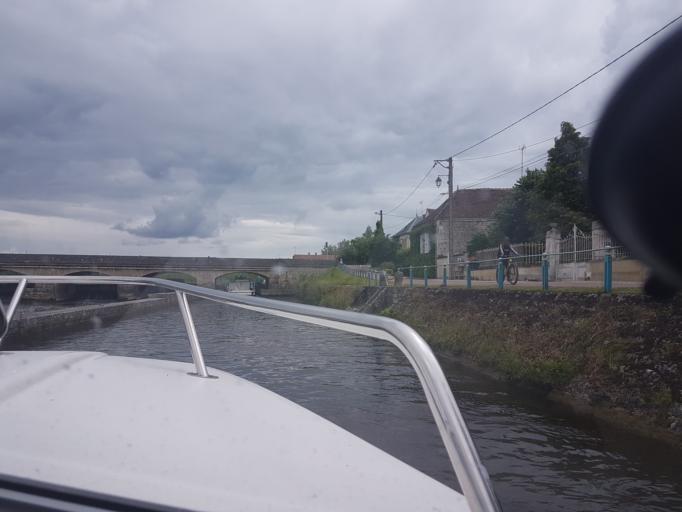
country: FR
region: Bourgogne
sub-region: Departement de l'Yonne
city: Champs-sur-Yonne
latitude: 47.7330
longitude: 3.6000
